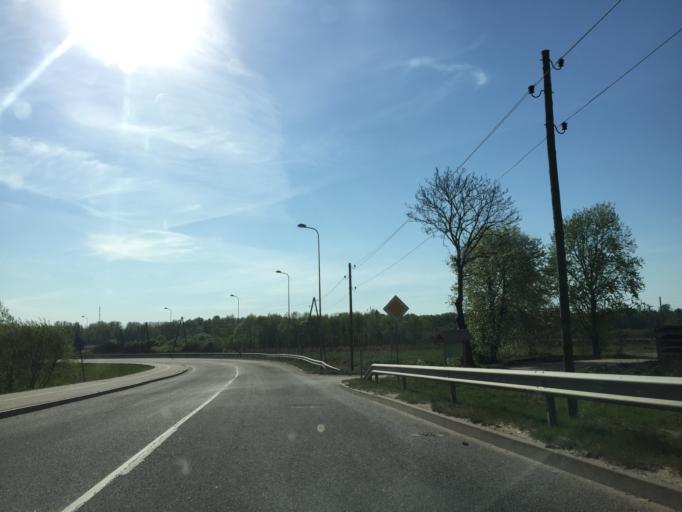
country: LV
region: Limbazu Rajons
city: Limbazi
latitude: 57.5172
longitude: 24.7088
